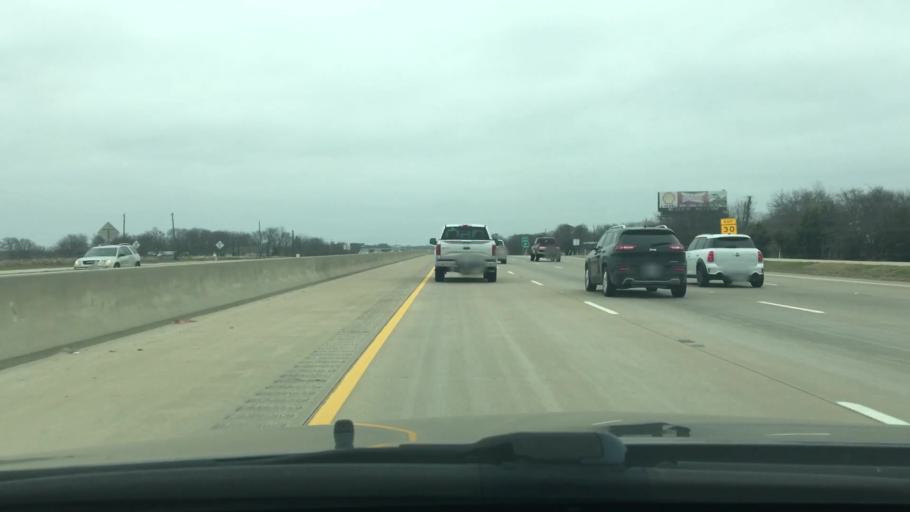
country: US
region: Texas
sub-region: Ellis County
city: Ennis
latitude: 32.2524
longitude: -96.5011
